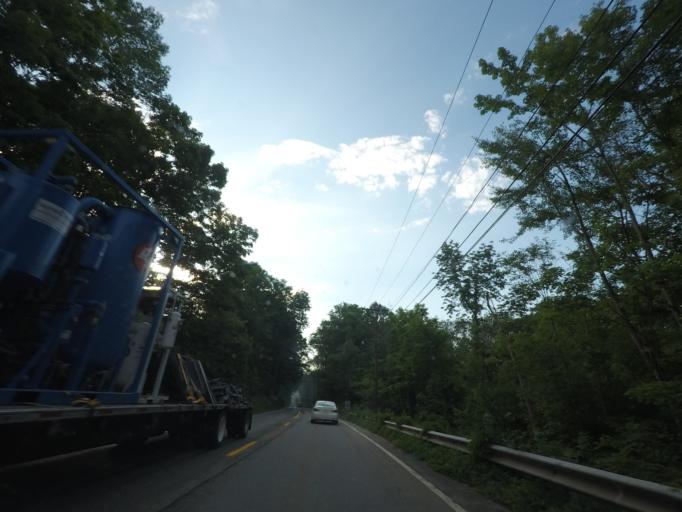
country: US
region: Connecticut
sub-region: Windham County
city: Quinebaug
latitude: 42.0496
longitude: -71.9853
